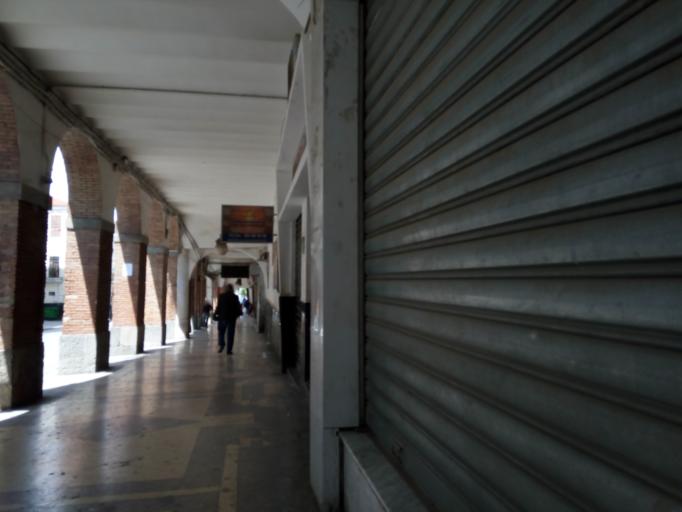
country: DZ
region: Constantine
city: Constantine
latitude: 36.3623
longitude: 6.6079
